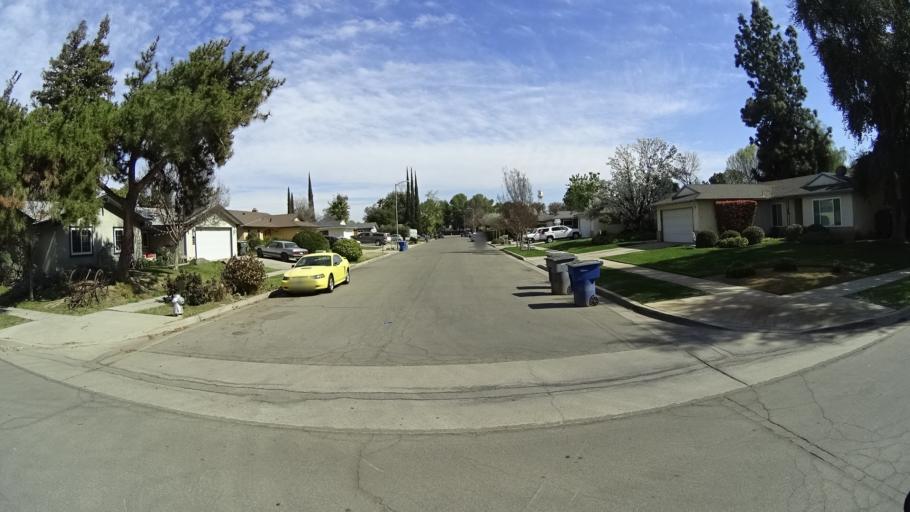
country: US
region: California
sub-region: Fresno County
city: Fresno
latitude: 36.8457
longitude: -119.8129
